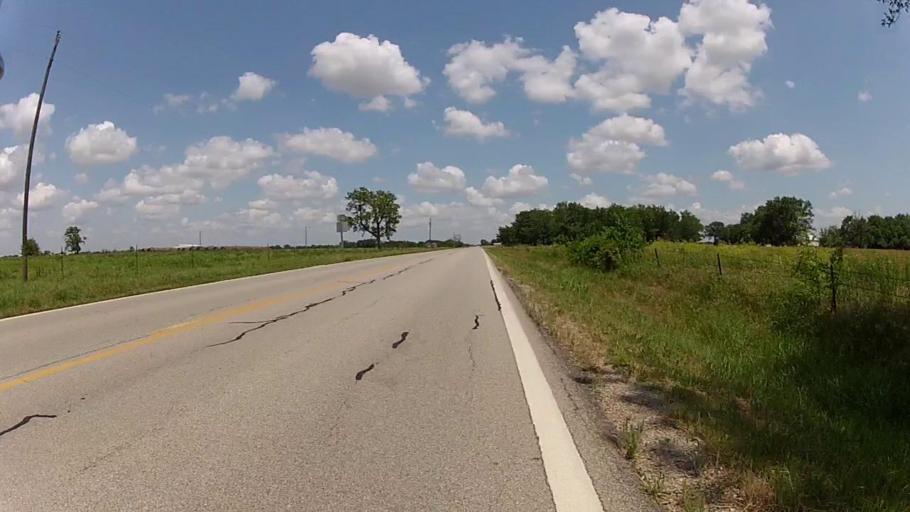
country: US
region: Kansas
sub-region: Labette County
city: Altamont
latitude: 37.1925
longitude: -95.3548
